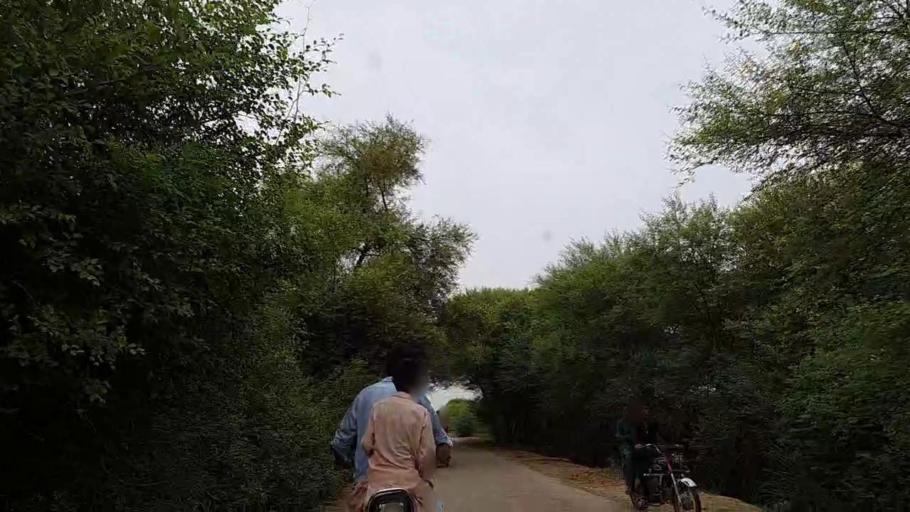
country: PK
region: Sindh
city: Mirpur Mathelo
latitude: 27.8504
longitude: 69.6296
